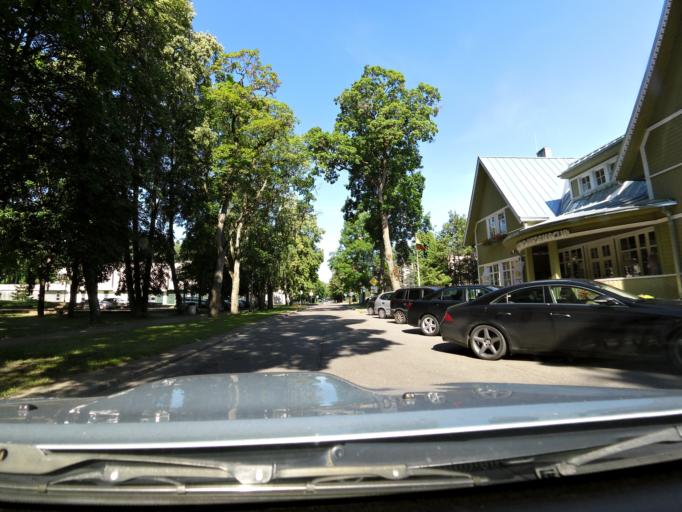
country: LT
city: Birstonas
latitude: 54.6002
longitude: 24.0327
